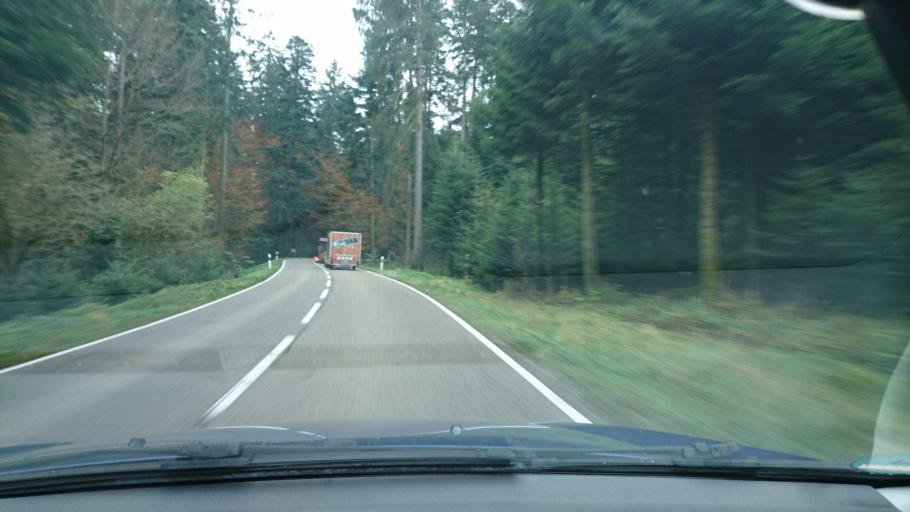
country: DE
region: Baden-Wuerttemberg
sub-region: Regierungsbezirk Stuttgart
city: Welzheim
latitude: 48.8988
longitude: 9.6627
